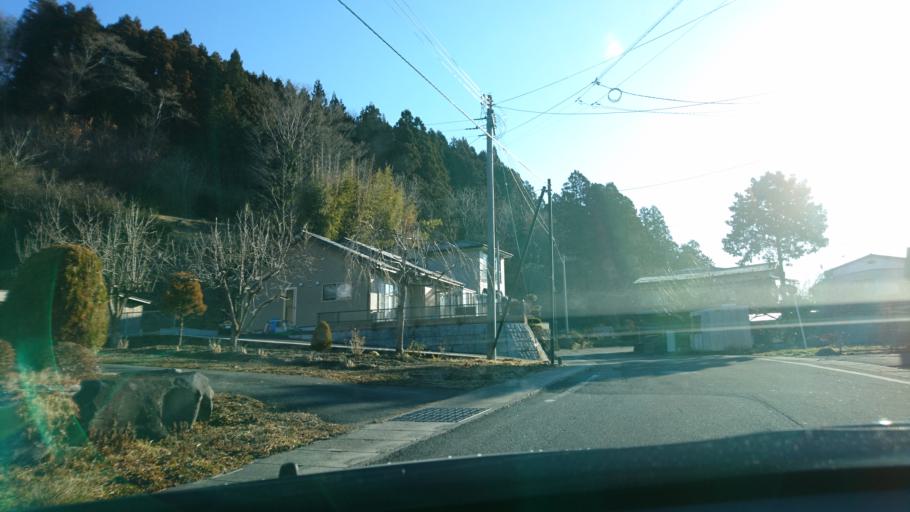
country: JP
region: Iwate
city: Ichinoseki
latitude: 38.9008
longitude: 141.2704
